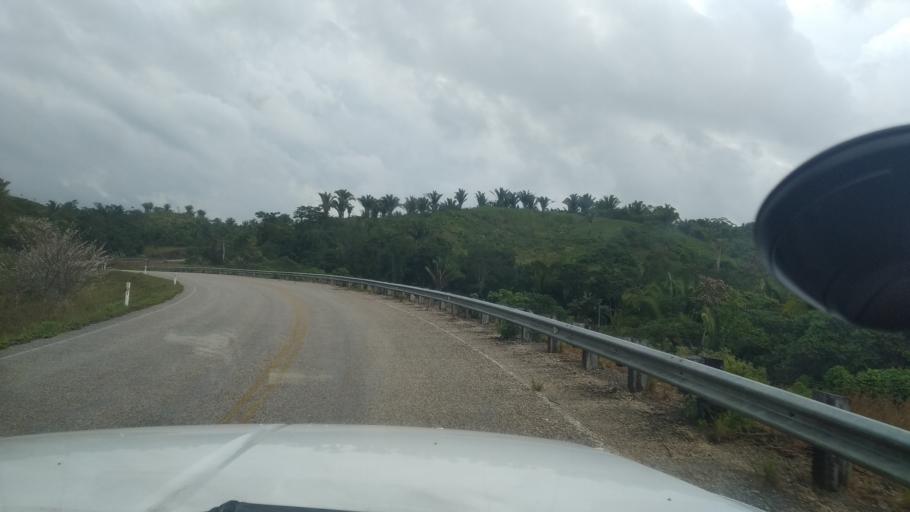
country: GT
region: Peten
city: San Luis
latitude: 16.1908
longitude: -89.1716
